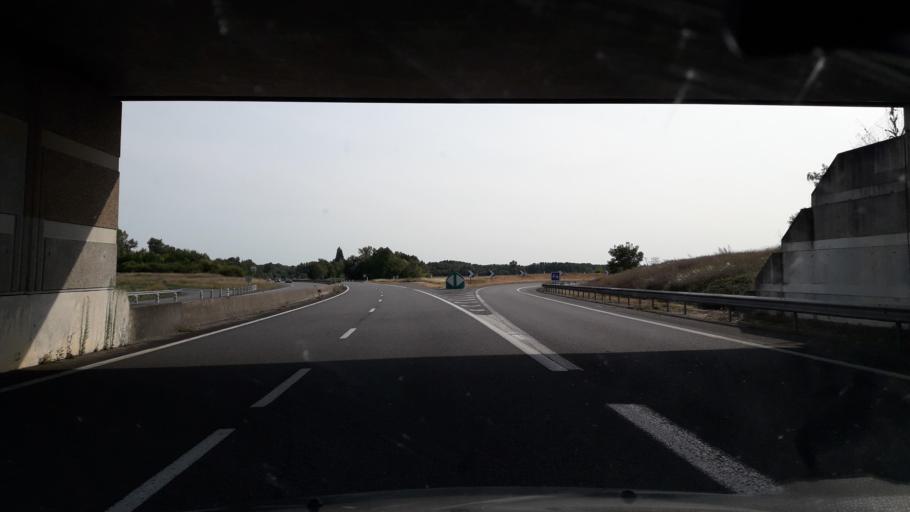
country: FR
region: Poitou-Charentes
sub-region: Departement de la Charente
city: Jarnac
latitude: 45.6929
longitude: -0.1361
